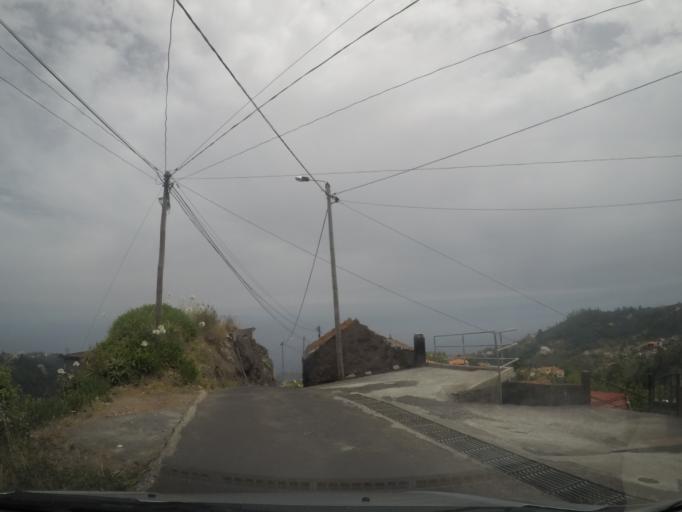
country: PT
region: Madeira
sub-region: Santa Cruz
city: Camacha
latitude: 32.6787
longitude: -16.8408
